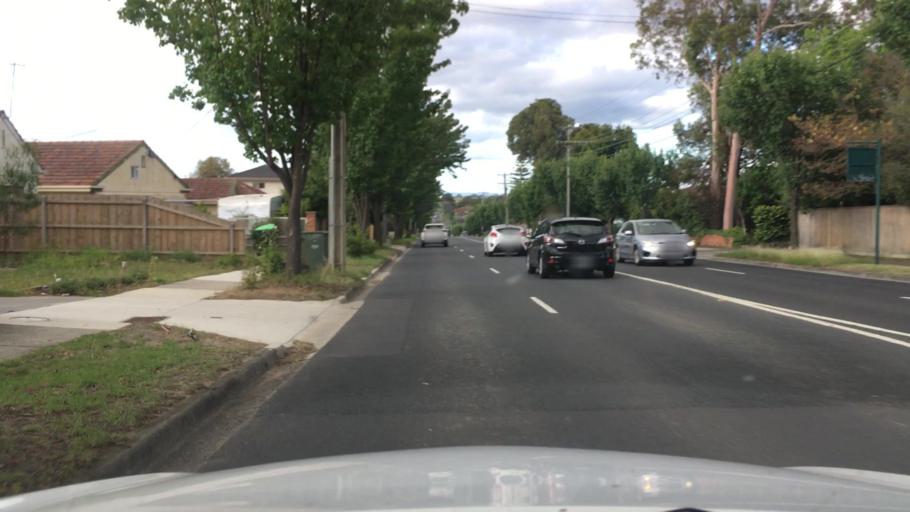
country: AU
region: Victoria
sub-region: Whitehorse
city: Burwood
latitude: -37.8451
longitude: 145.1336
